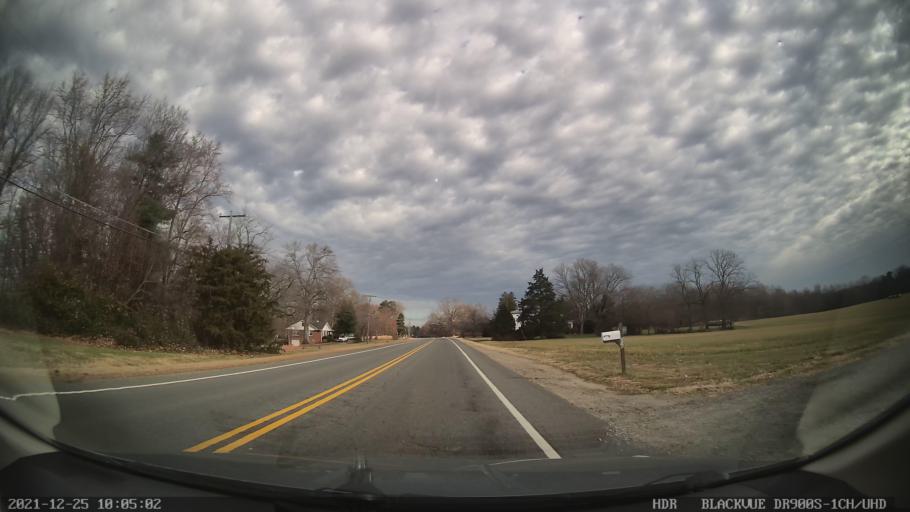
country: US
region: Virginia
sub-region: Louisa County
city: Louisa
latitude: 38.0194
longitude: -77.9021
